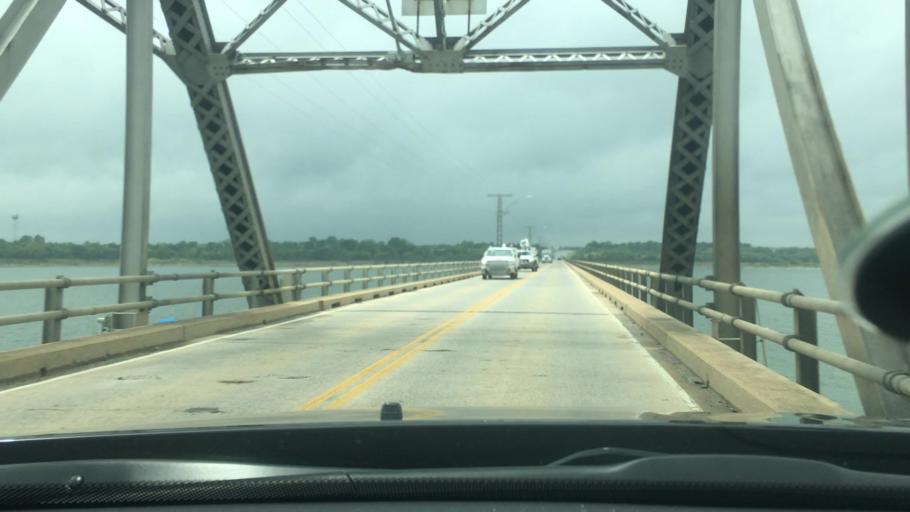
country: US
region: Oklahoma
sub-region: Marshall County
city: Kingston
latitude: 34.0010
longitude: -96.6218
